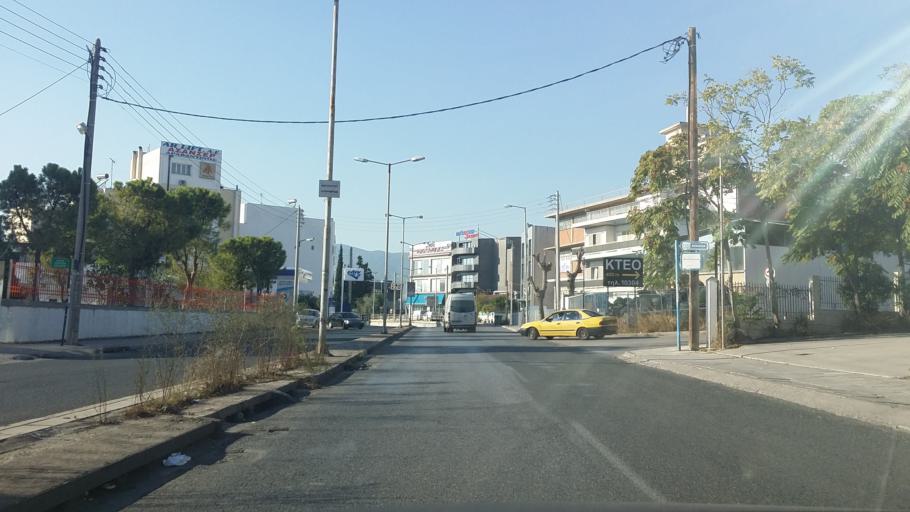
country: GR
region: Attica
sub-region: Nomarchia Athinas
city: Irakleio
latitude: 38.0538
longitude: 23.7472
